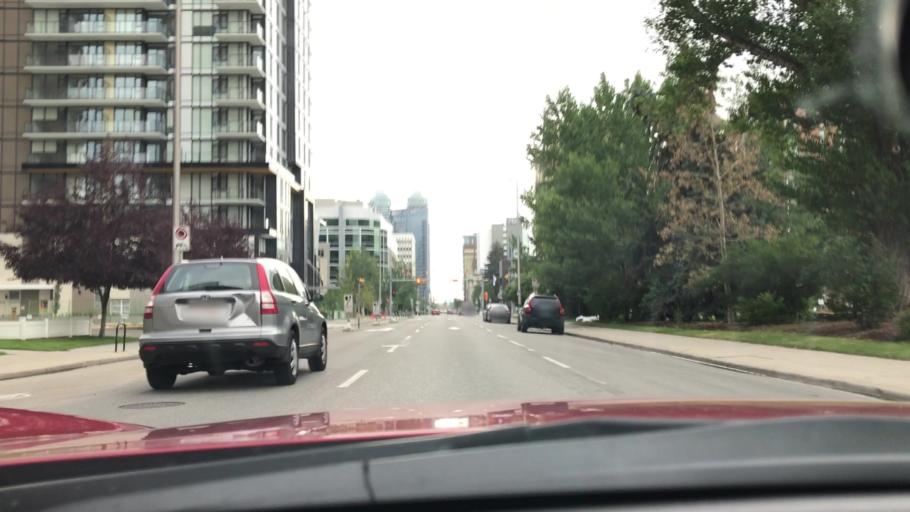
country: CA
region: Alberta
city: Calgary
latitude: 51.0416
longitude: -114.0701
